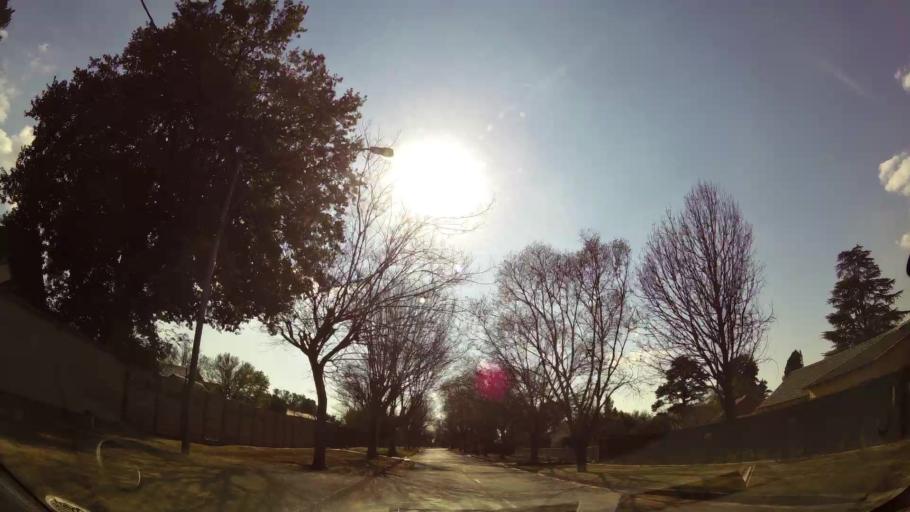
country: ZA
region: Gauteng
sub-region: Ekurhuleni Metropolitan Municipality
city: Benoni
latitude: -26.1501
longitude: 28.3411
